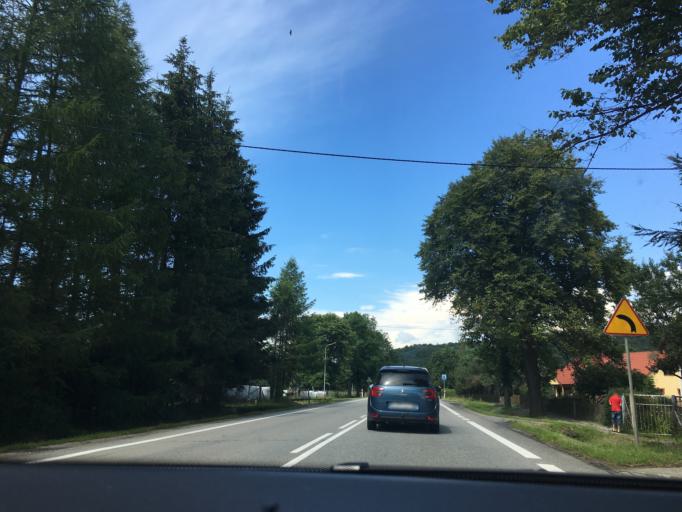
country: PL
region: Subcarpathian Voivodeship
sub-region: Powiat krosnienski
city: Jasliska
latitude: 49.4346
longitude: 21.6895
